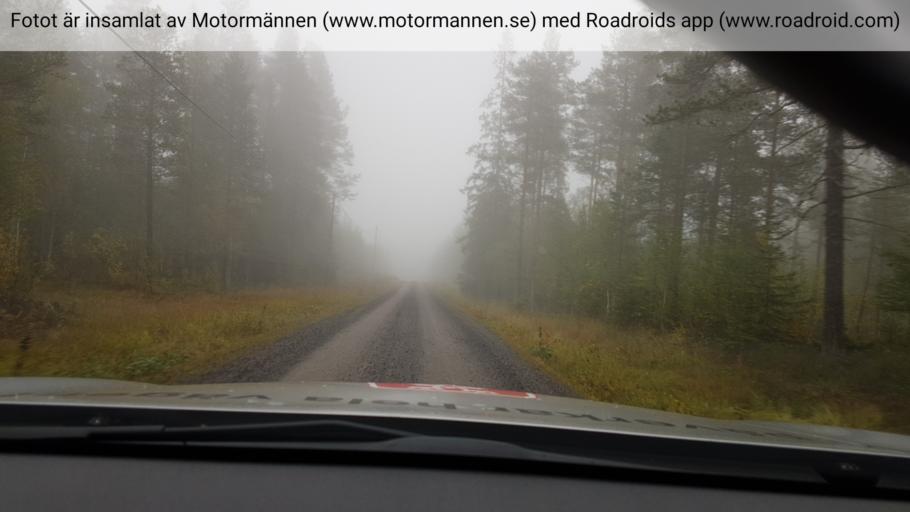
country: SE
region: Vaesterbotten
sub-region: Skelleftea Kommun
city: Burtraesk
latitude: 64.2967
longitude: 20.4116
